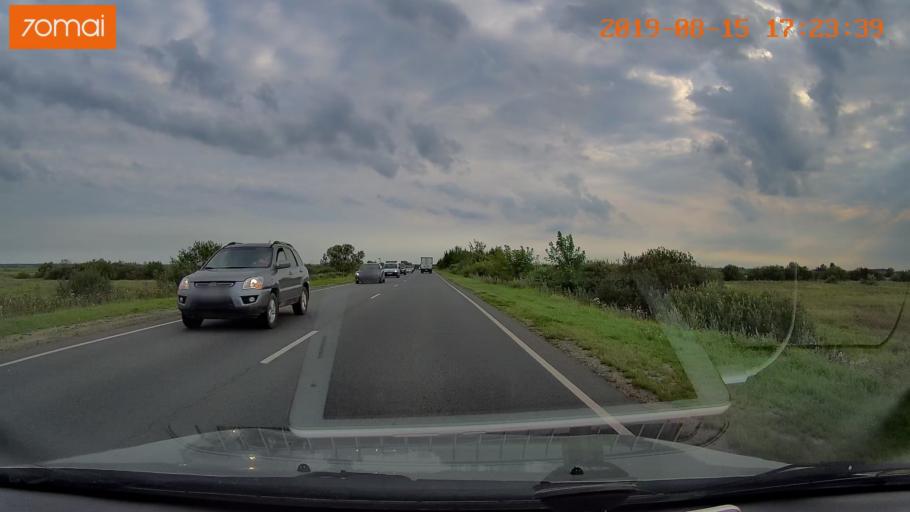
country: RU
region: Moskovskaya
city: Ashitkovo
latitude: 55.3982
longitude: 38.5547
